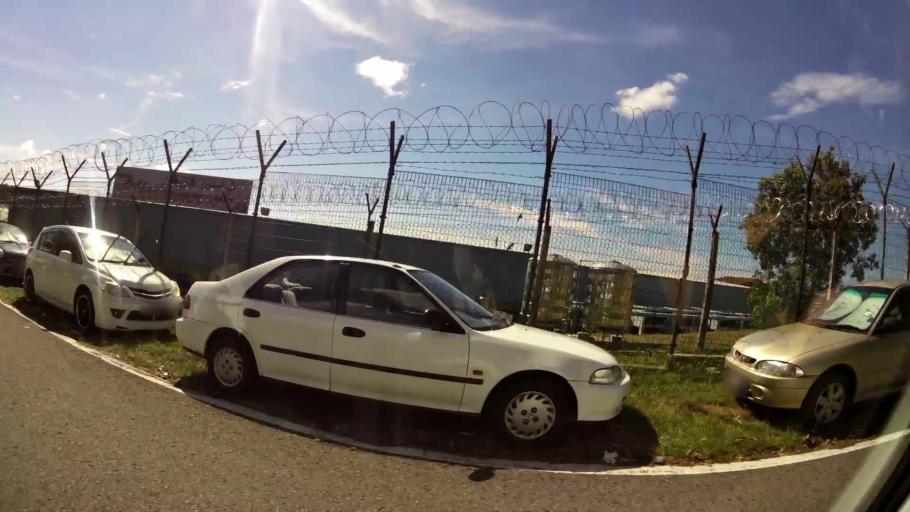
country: BN
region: Brunei and Muara
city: Bandar Seri Begawan
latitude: 4.9507
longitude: 114.9364
